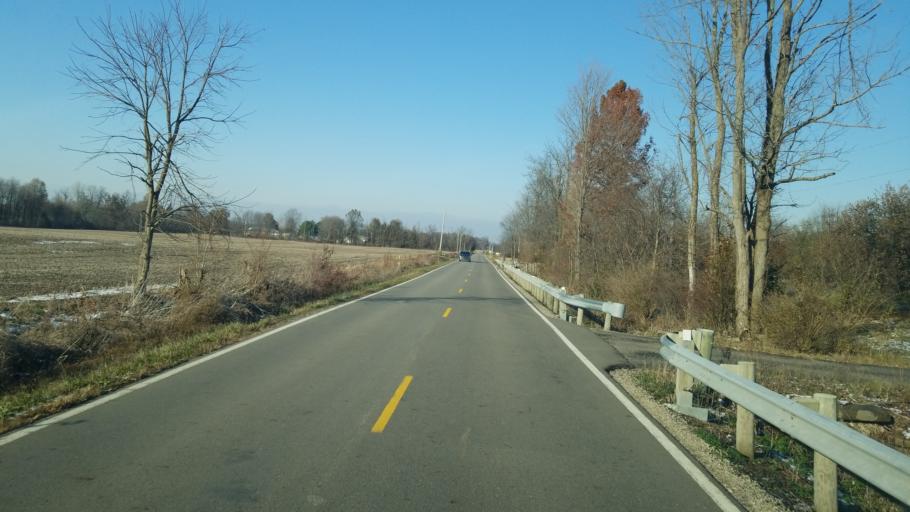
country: US
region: Ohio
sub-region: Licking County
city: Johnstown
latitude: 40.1808
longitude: -82.6110
